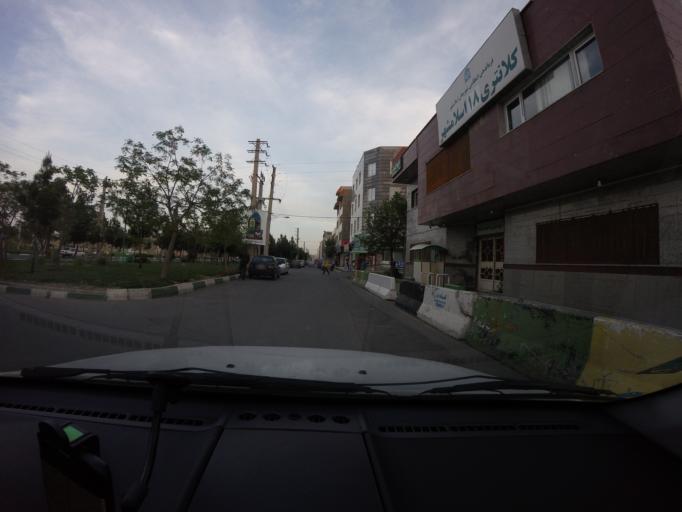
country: IR
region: Tehran
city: Eslamshahr
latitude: 35.5363
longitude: 51.2126
